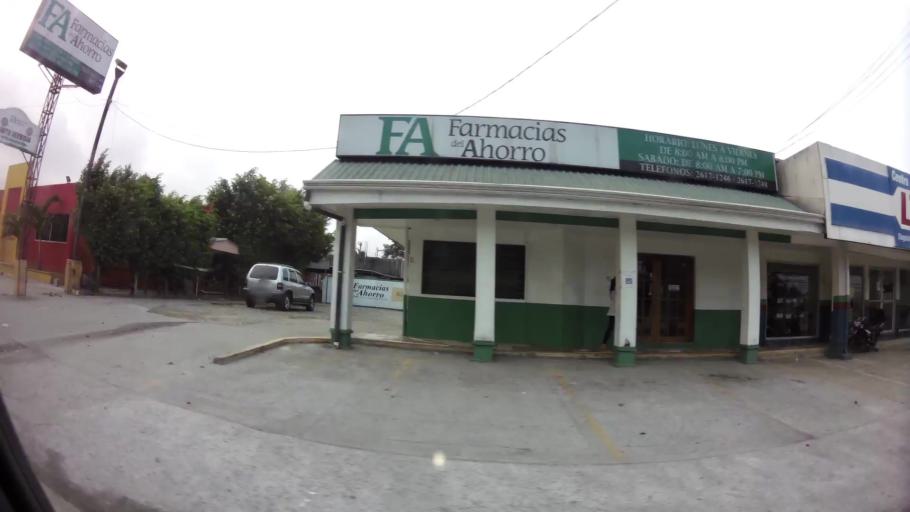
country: HN
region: Yoro
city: El Progreso
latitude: 15.4045
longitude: -87.8090
